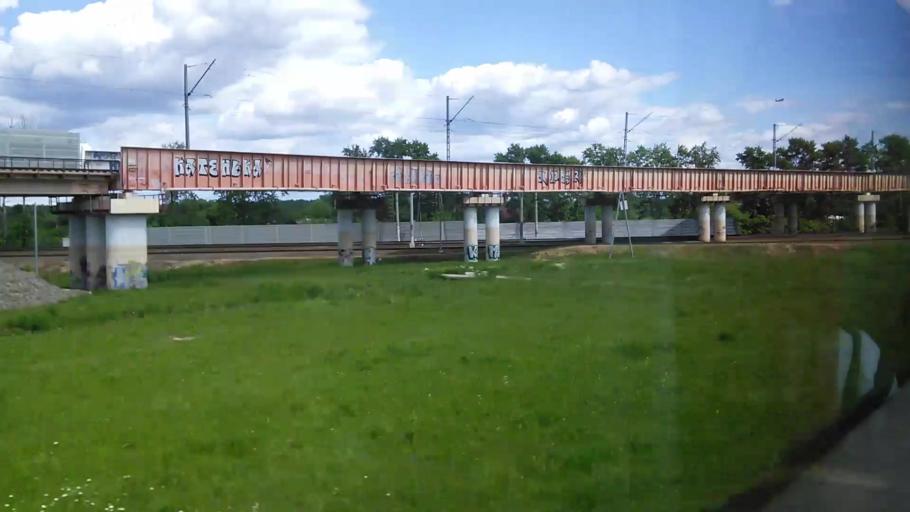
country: RU
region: Moskovskaya
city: Lobnya
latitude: 55.9980
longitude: 37.4905
